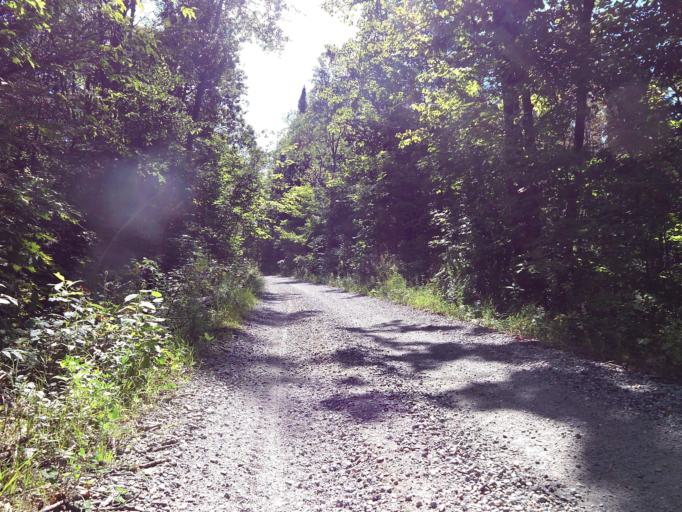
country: CA
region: Ontario
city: Renfrew
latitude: 45.0339
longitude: -76.7062
